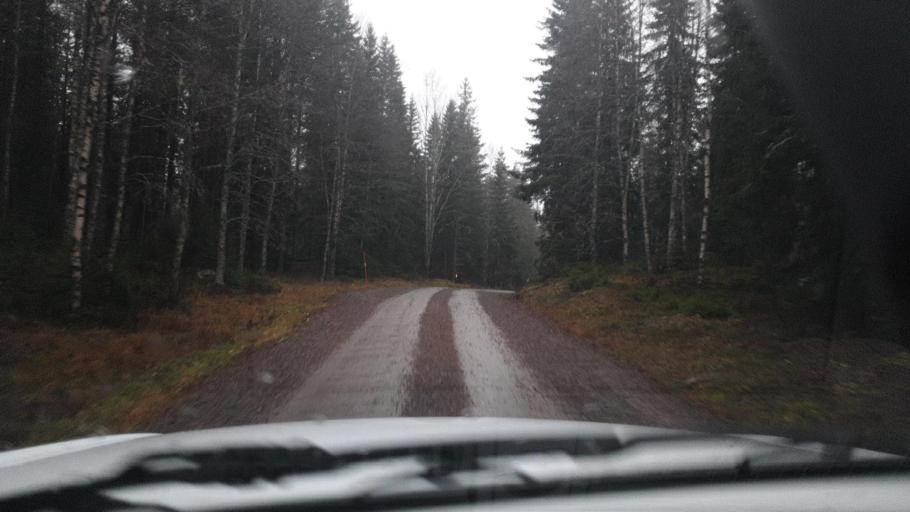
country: SE
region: Vaermland
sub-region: Arvika Kommun
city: Arvika
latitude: 59.9800
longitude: 12.6609
